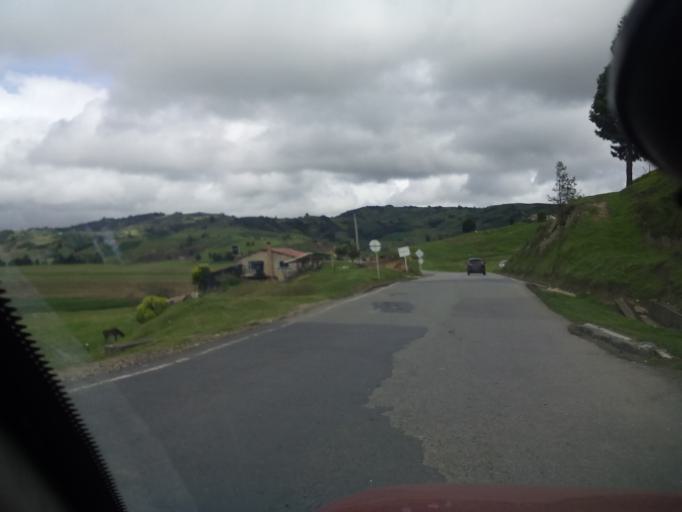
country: CO
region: Boyaca
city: Combita
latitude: 5.6586
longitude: -73.3558
